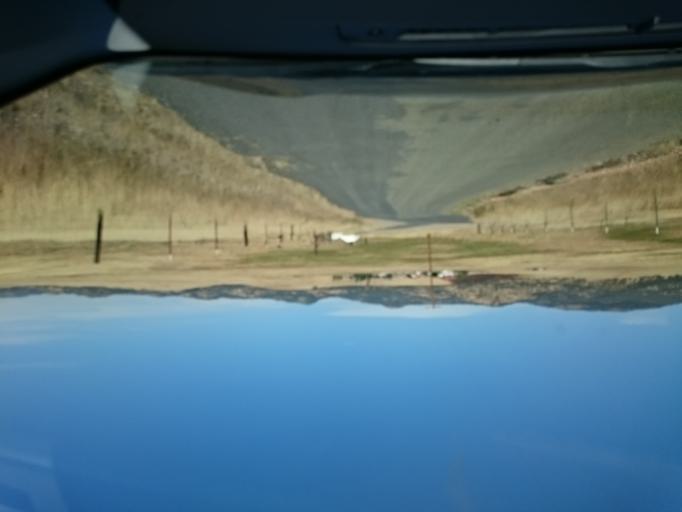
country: US
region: California
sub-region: Calaveras County
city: Copperopolis
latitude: 38.0538
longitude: -120.7358
